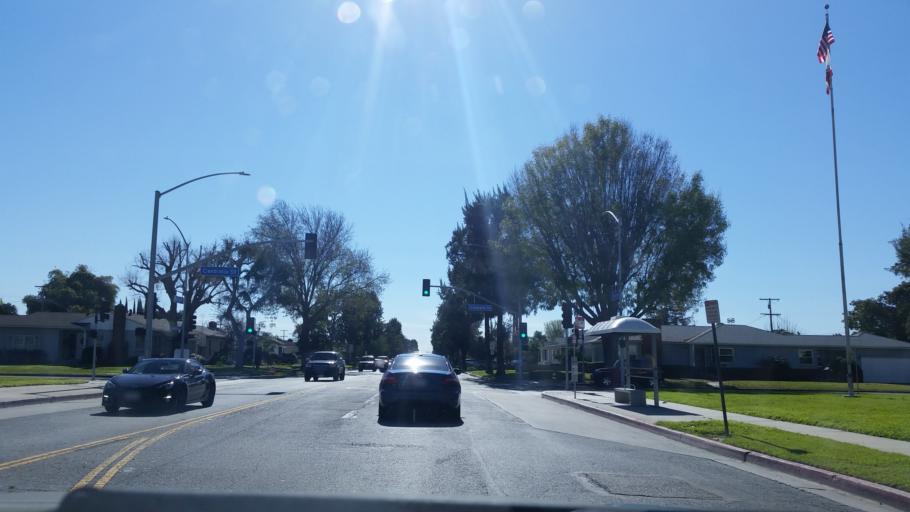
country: US
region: California
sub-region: Los Angeles County
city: Lakewood
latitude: 33.8401
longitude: -118.1339
